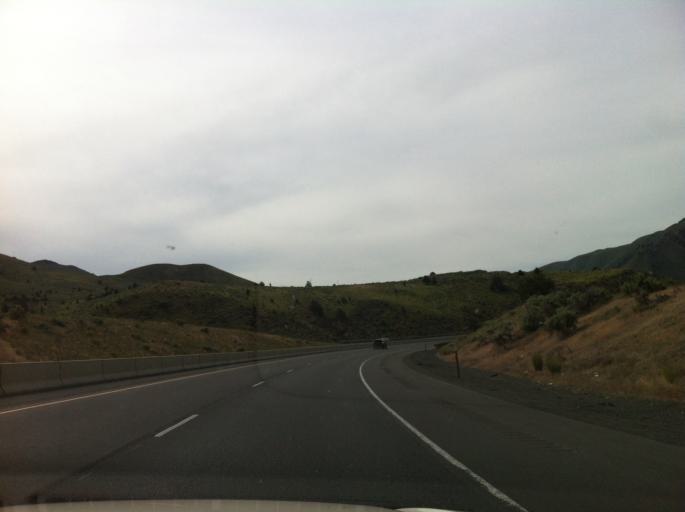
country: US
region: Idaho
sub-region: Washington County
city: Weiser
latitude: 44.5181
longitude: -117.3758
